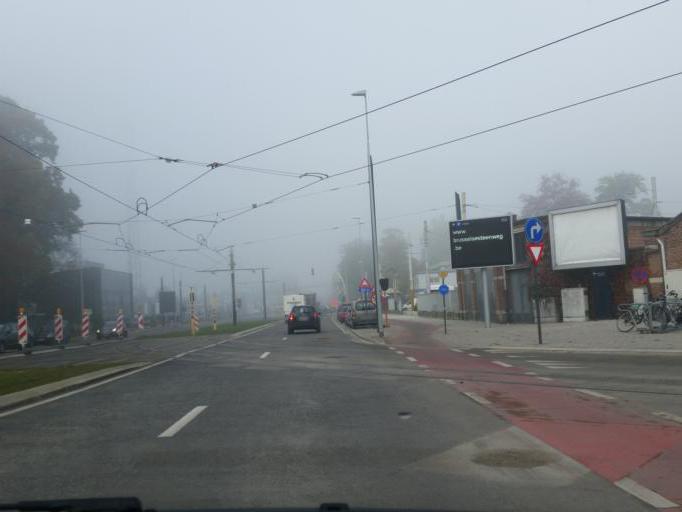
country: BE
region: Flanders
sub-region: Provincie Oost-Vlaanderen
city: Ledeberg
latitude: 51.0358
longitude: 3.7528
